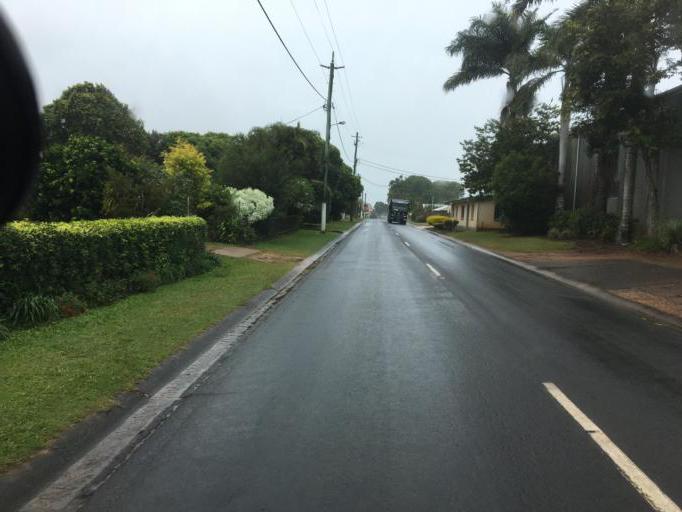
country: AU
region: Queensland
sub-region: Tablelands
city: Tolga
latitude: -17.2157
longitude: 145.5401
